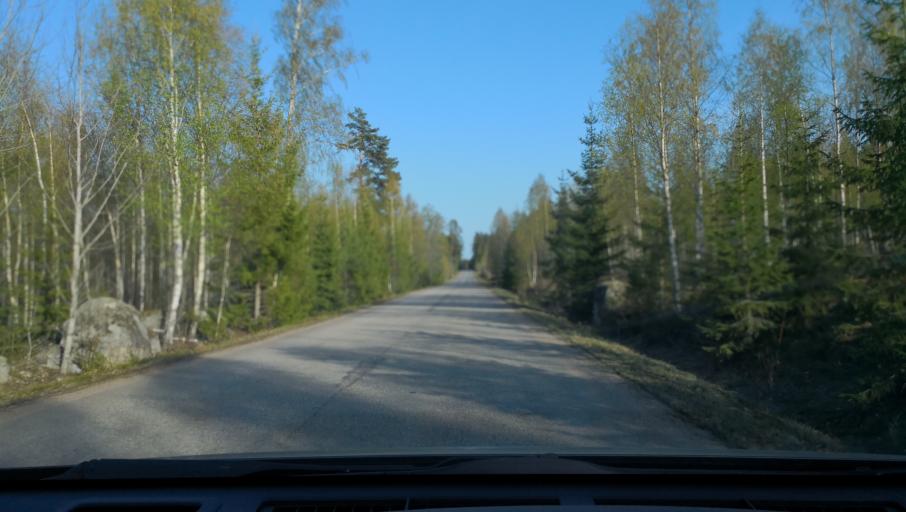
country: SE
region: Uppsala
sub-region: Heby Kommun
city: Tarnsjo
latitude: 60.2630
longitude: 16.9309
